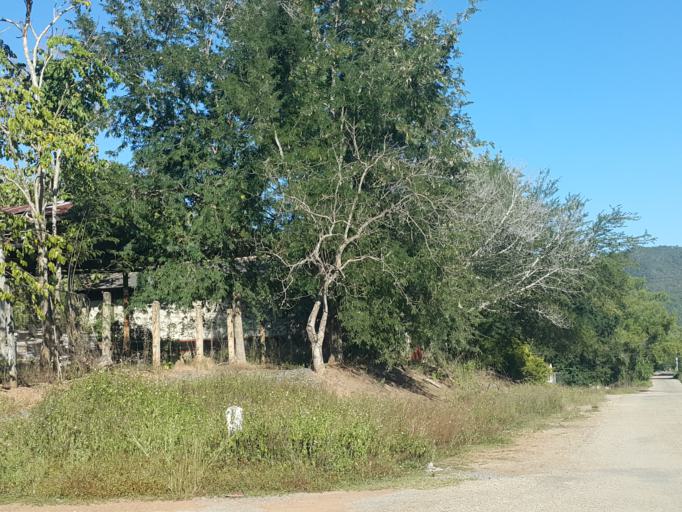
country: TH
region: Chiang Mai
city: San Sai
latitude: 18.9248
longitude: 99.1298
